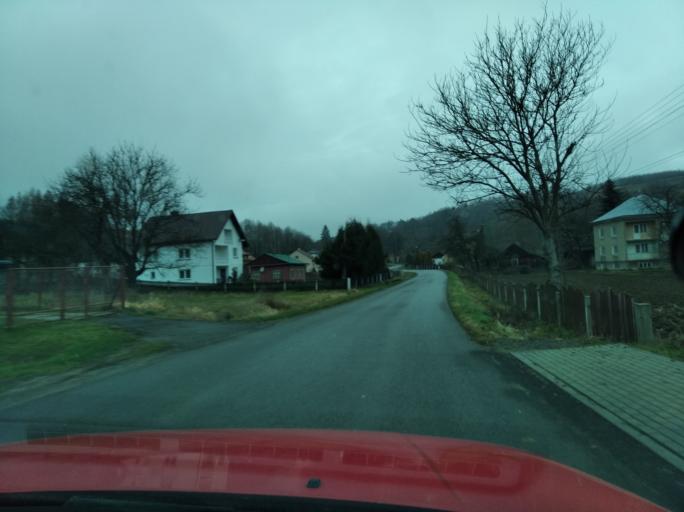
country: PL
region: Subcarpathian Voivodeship
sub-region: Powiat przemyski
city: Nienadowa
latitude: 49.8465
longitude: 22.4301
